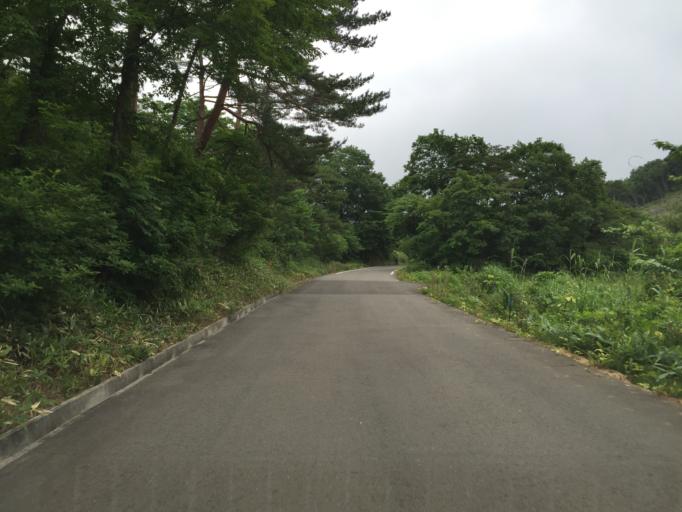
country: JP
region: Miyagi
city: Marumori
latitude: 37.8036
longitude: 140.7500
